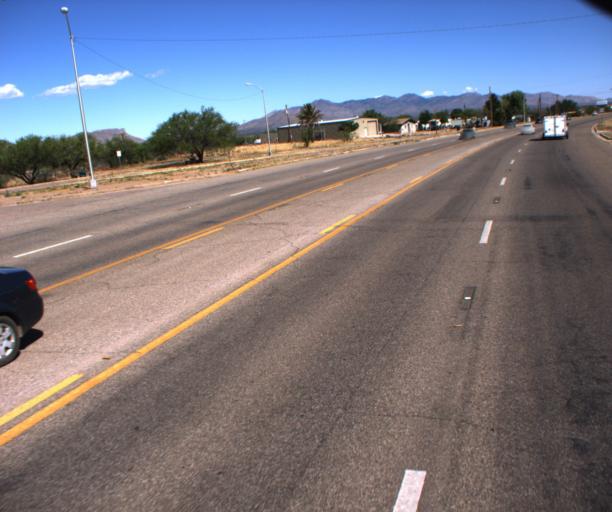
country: US
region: Arizona
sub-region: Cochise County
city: Huachuca City
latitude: 31.6184
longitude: -110.3354
